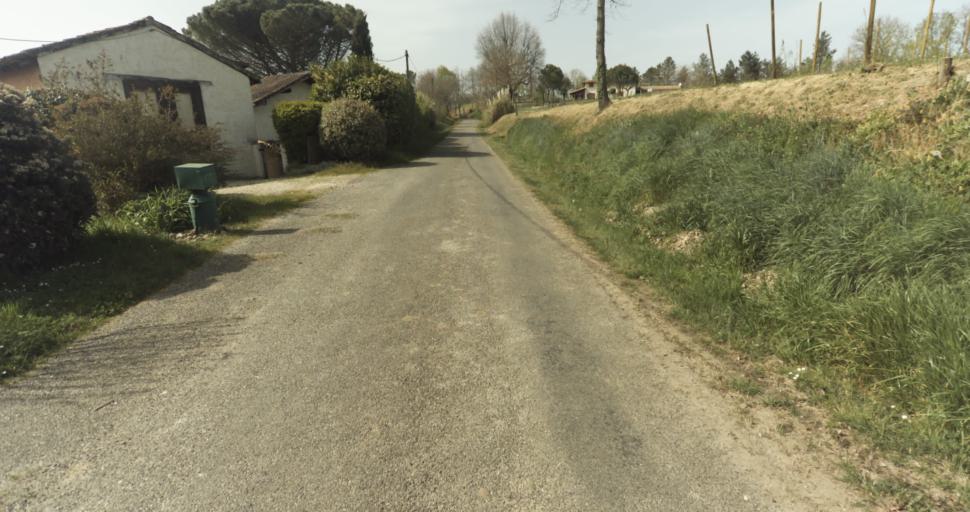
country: FR
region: Midi-Pyrenees
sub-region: Departement du Tarn-et-Garonne
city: Moissac
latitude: 44.1423
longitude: 1.1495
